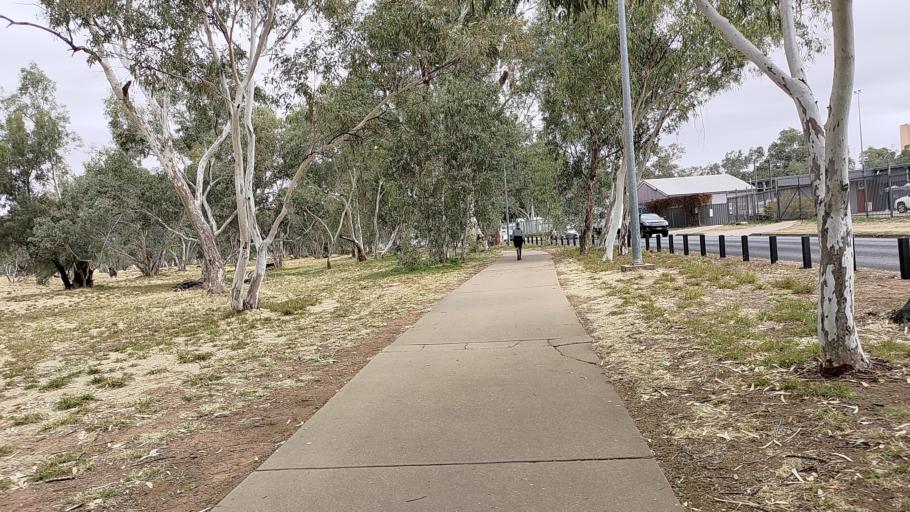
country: AU
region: Northern Territory
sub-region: Alice Springs
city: Alice Springs
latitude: -23.7045
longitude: 133.8816
